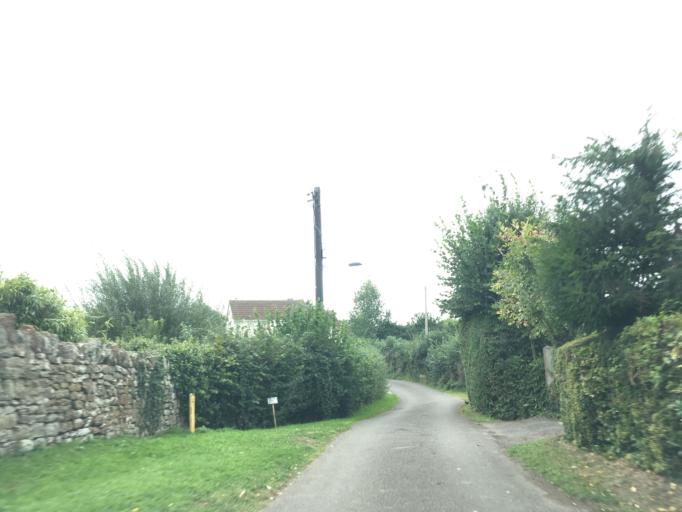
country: GB
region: England
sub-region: South Gloucestershire
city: Thornbury
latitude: 51.6112
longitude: -2.5001
